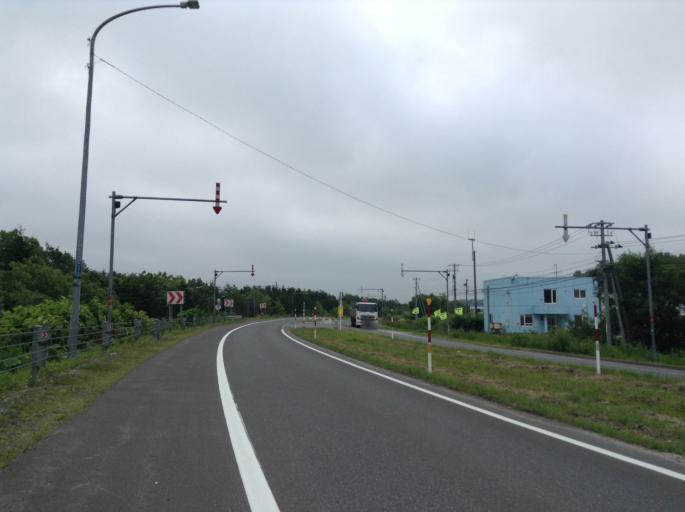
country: JP
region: Hokkaido
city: Wakkanai
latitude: 45.3689
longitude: 141.7266
